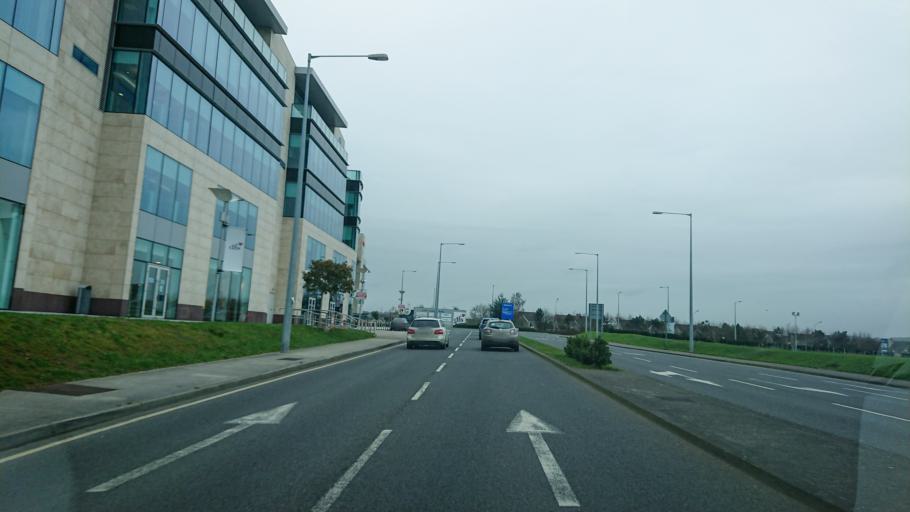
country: IE
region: Munster
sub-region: County Cork
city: Passage West
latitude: 51.8858
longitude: -8.4016
